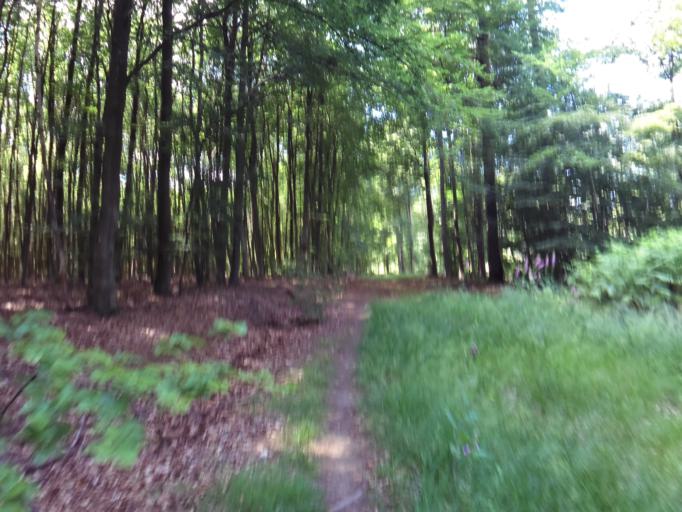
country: DE
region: Rheinland-Pfalz
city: Waldleiningen
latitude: 49.3687
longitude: 7.8514
